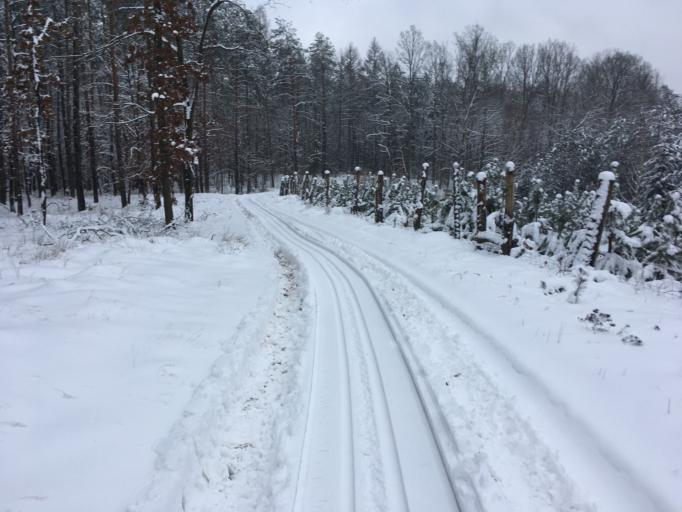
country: PL
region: Kujawsko-Pomorskie
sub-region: Powiat brodnicki
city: Gorzno
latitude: 53.1908
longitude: 19.6858
